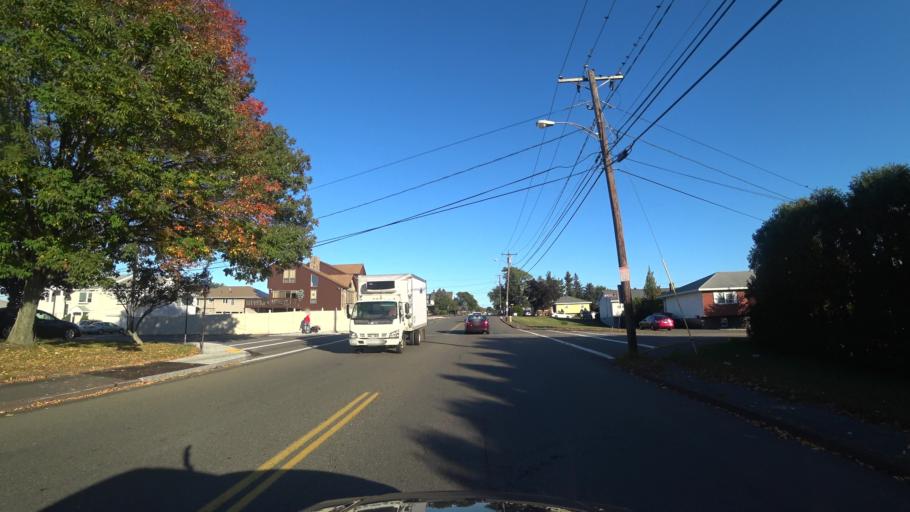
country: US
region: Massachusetts
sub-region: Suffolk County
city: Revere
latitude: 42.4208
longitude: -71.0258
